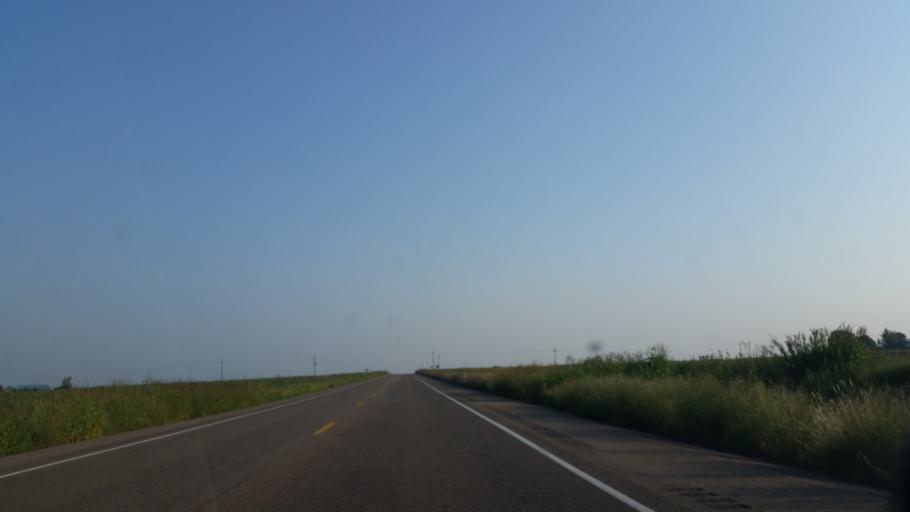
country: US
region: New Mexico
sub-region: Curry County
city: Clovis
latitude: 34.5467
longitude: -103.1965
